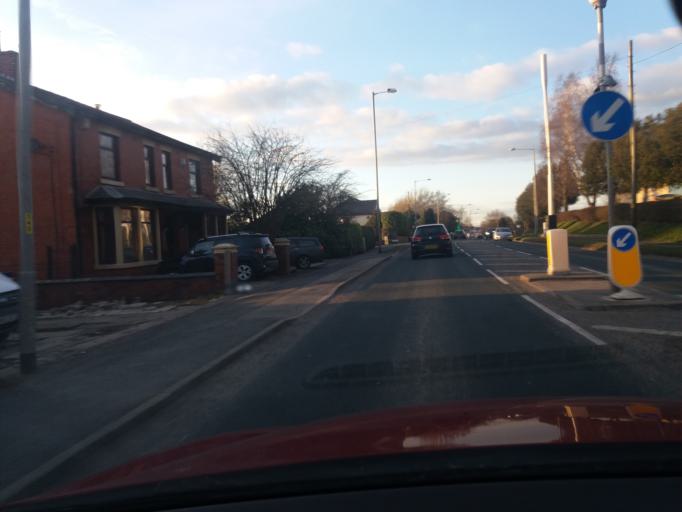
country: GB
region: England
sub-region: Lancashire
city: Chorley
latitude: 53.6748
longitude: -2.6349
